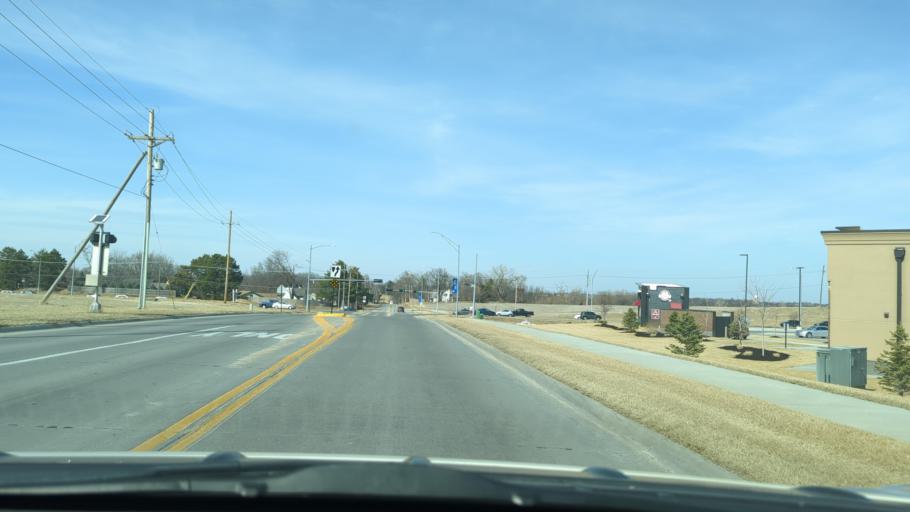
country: US
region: Nebraska
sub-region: Sarpy County
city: Papillion
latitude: 41.1385
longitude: -96.0524
